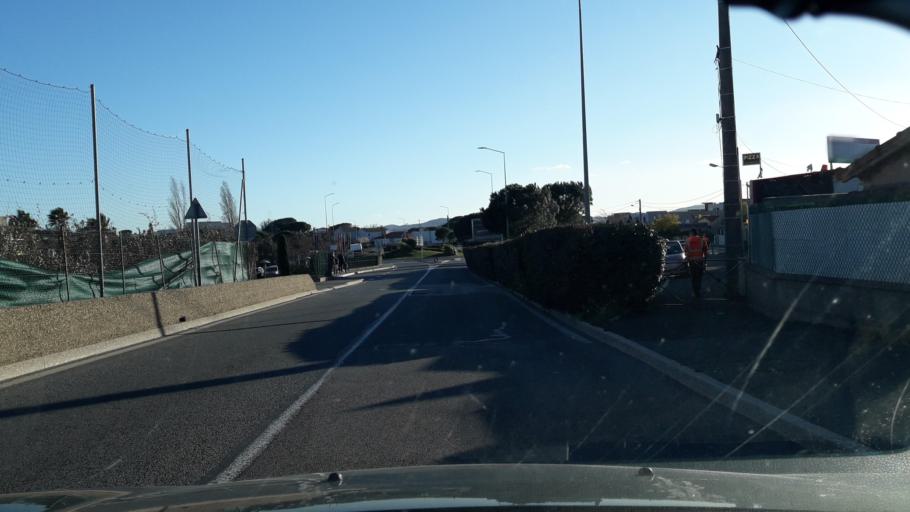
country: FR
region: Provence-Alpes-Cote d'Azur
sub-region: Departement du Var
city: Frejus
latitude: 43.4547
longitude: 6.7272
